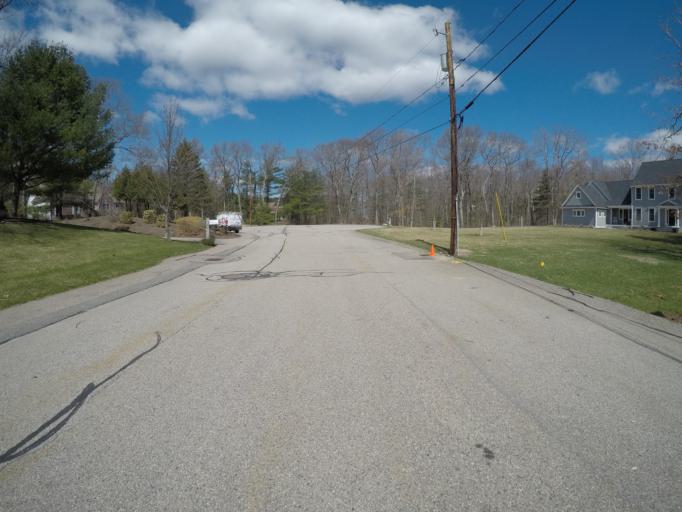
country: US
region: Massachusetts
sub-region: Bristol County
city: Easton
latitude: 42.0707
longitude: -71.1347
